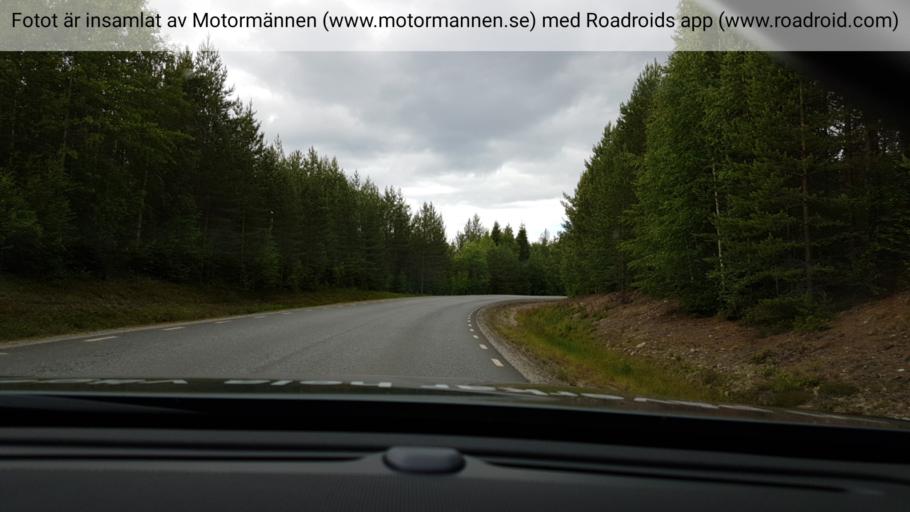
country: SE
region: Vaesterbotten
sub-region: Vindelns Kommun
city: Vindeln
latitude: 64.1790
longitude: 19.6730
